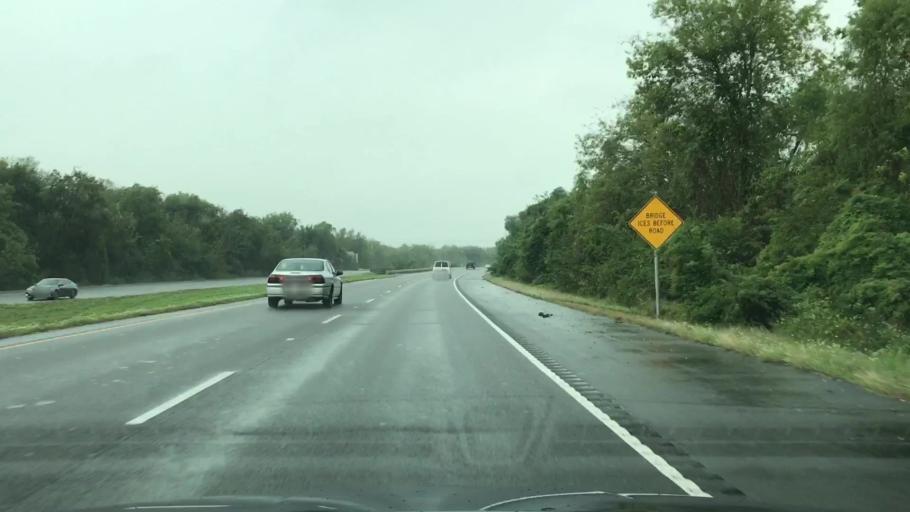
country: US
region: Louisiana
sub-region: Lafourche Parish
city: Raceland
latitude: 29.6935
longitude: -90.5862
